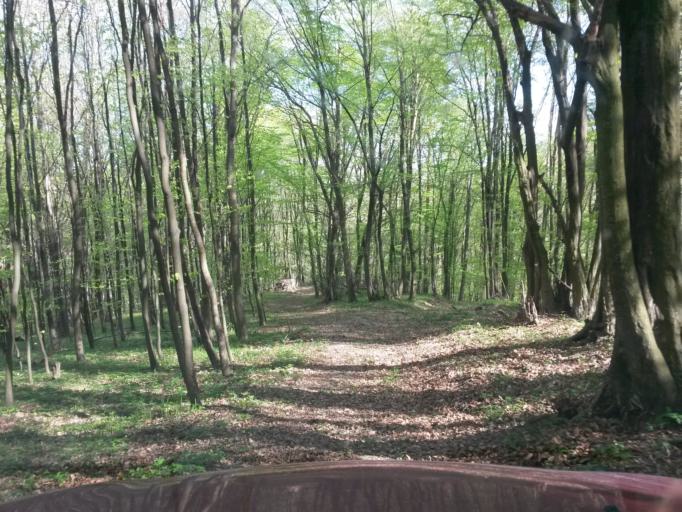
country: SK
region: Presovsky
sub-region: Okres Presov
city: Presov
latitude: 48.9477
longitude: 21.1588
